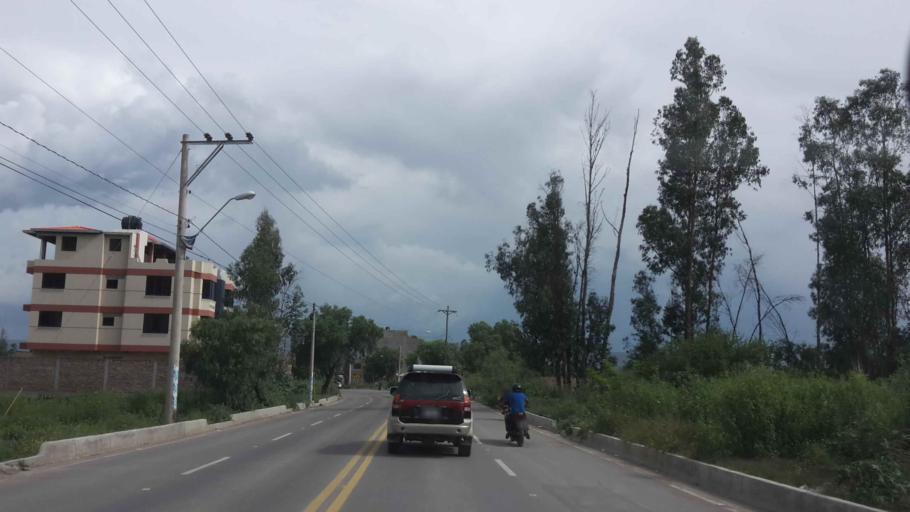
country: BO
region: Cochabamba
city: Cochabamba
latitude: -17.3544
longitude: -66.2547
